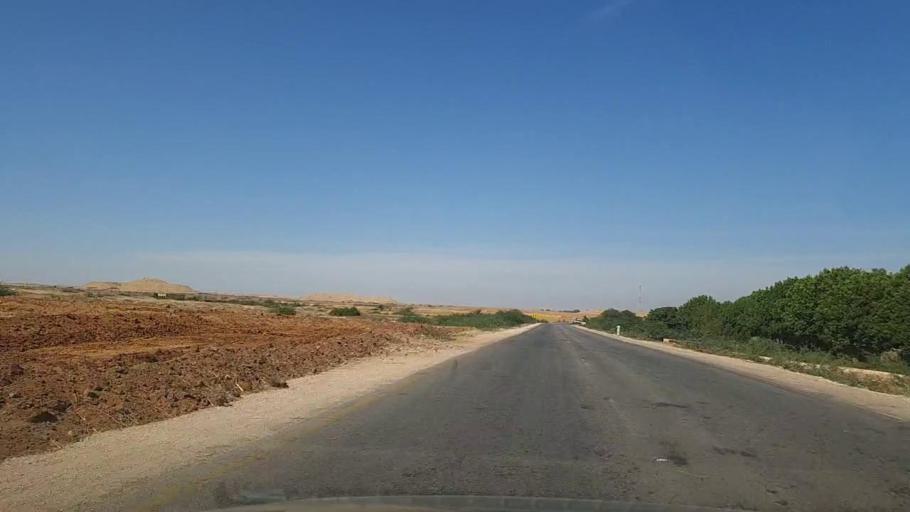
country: PK
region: Sindh
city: Kotri
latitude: 25.1895
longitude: 68.2396
